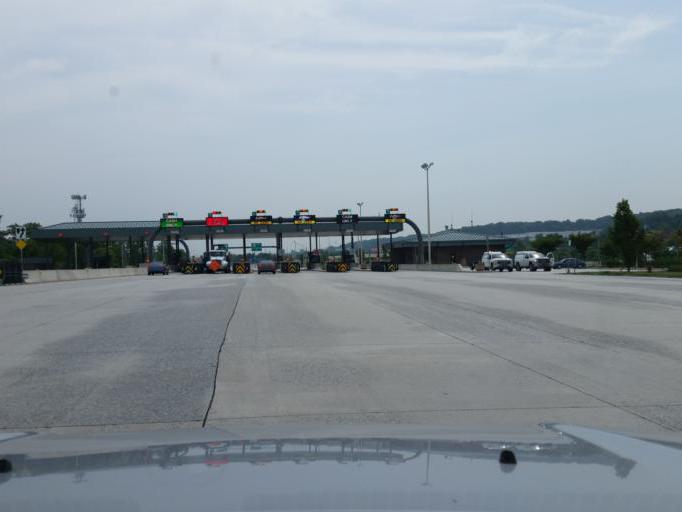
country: US
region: Pennsylvania
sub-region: Cumberland County
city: Mechanicsburg
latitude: 40.1973
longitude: -76.9775
